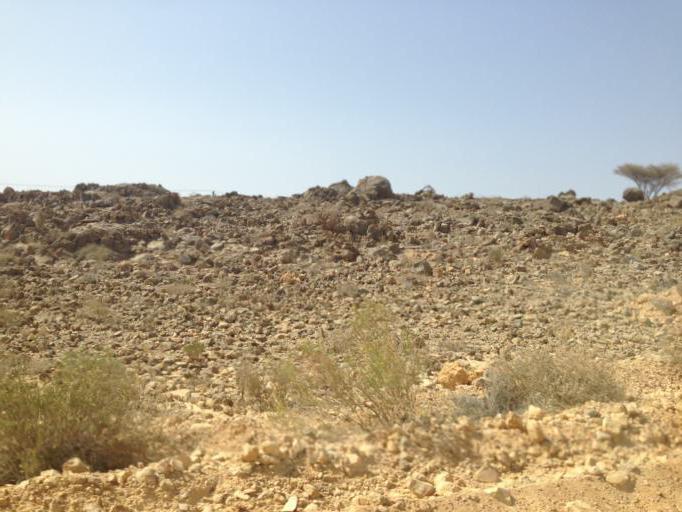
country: OM
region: Ash Sharqiyah
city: Ibra'
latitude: 23.0850
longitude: 58.9440
